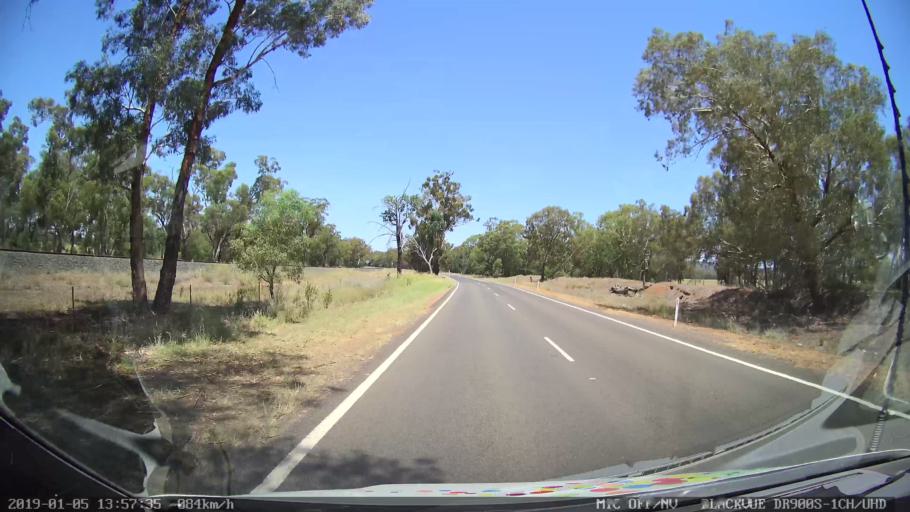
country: AU
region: New South Wales
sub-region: Gunnedah
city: Gunnedah
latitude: -31.1293
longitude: 150.2755
